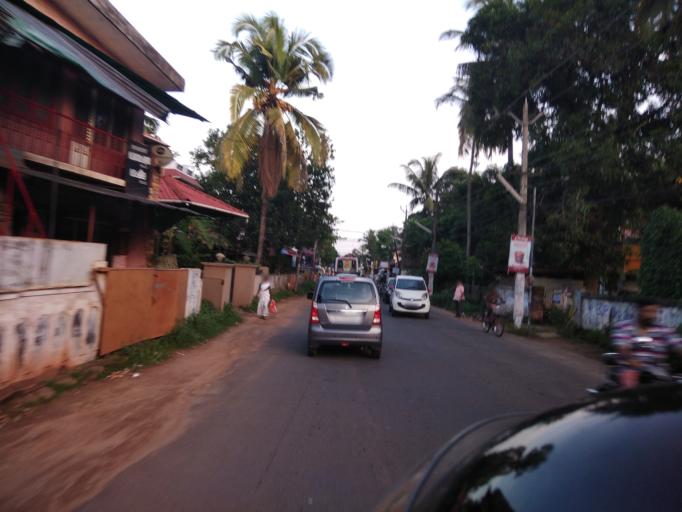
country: IN
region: Kerala
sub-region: Thrissur District
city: Trichur
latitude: 10.5310
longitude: 76.1851
